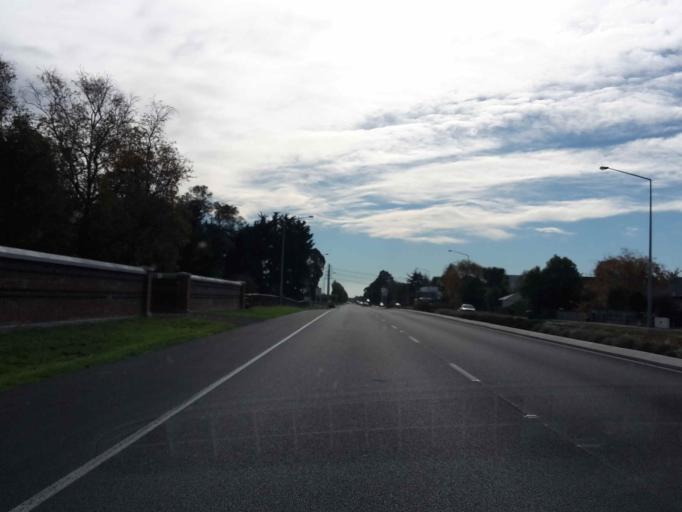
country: NZ
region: Canterbury
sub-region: Selwyn District
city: Prebbleton
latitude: -43.5165
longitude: 172.5363
